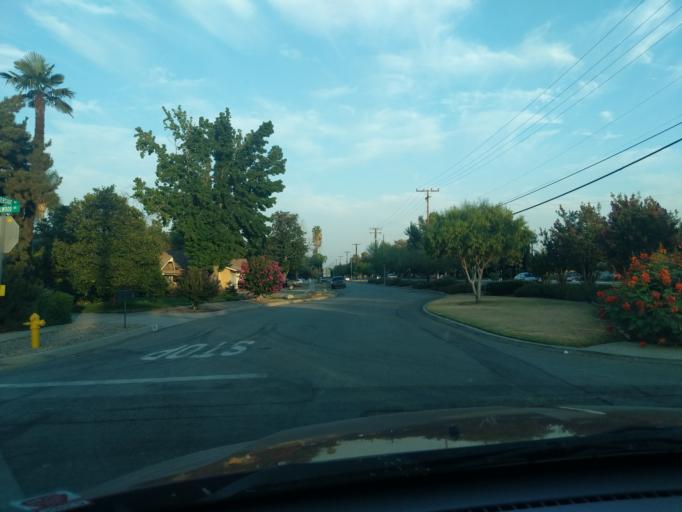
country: US
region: California
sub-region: San Bernardino County
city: Muscoy
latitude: 34.1494
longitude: -117.3878
